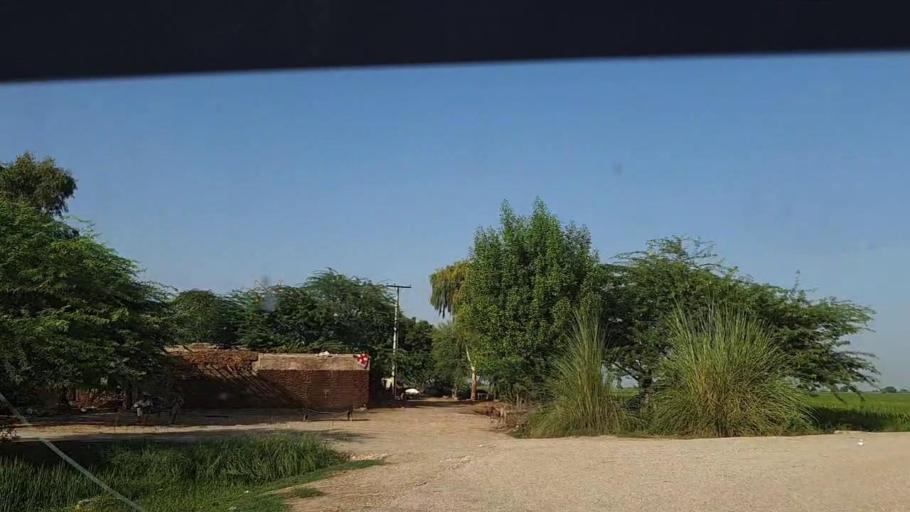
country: PK
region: Sindh
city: Tangwani
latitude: 28.2660
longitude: 69.0128
